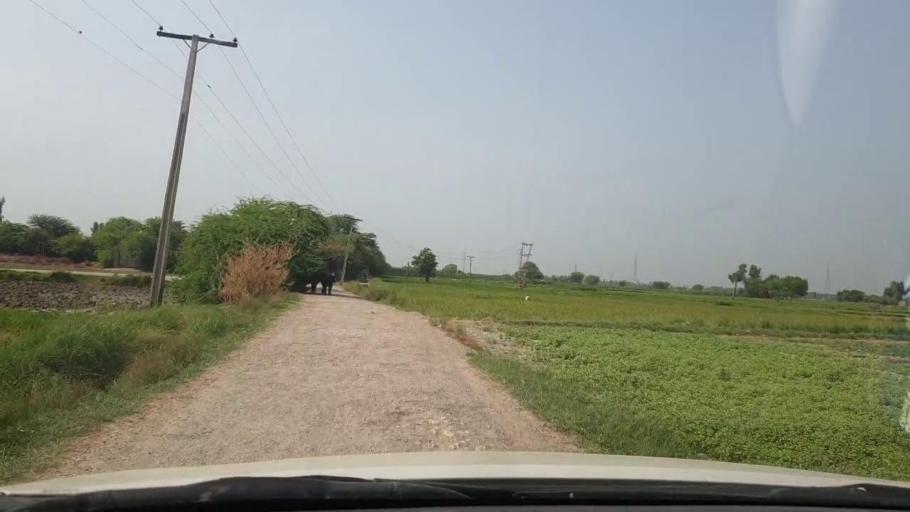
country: PK
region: Sindh
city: Shikarpur
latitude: 27.9824
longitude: 68.6723
